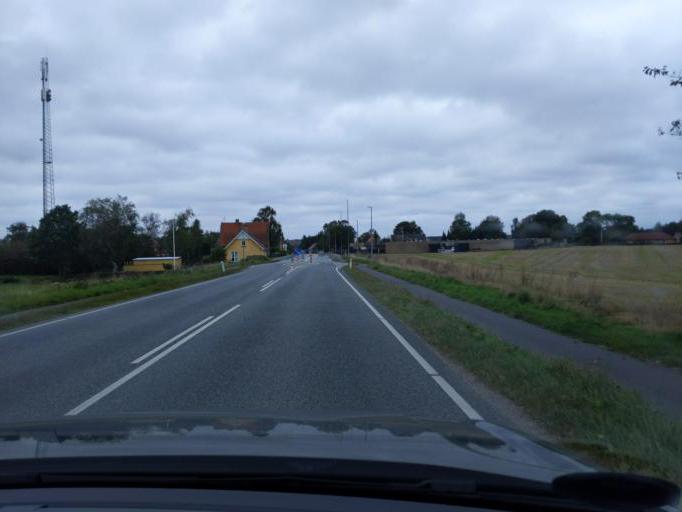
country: DK
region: Central Jutland
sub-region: Randers Kommune
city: Spentrup
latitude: 56.5106
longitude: 9.9525
